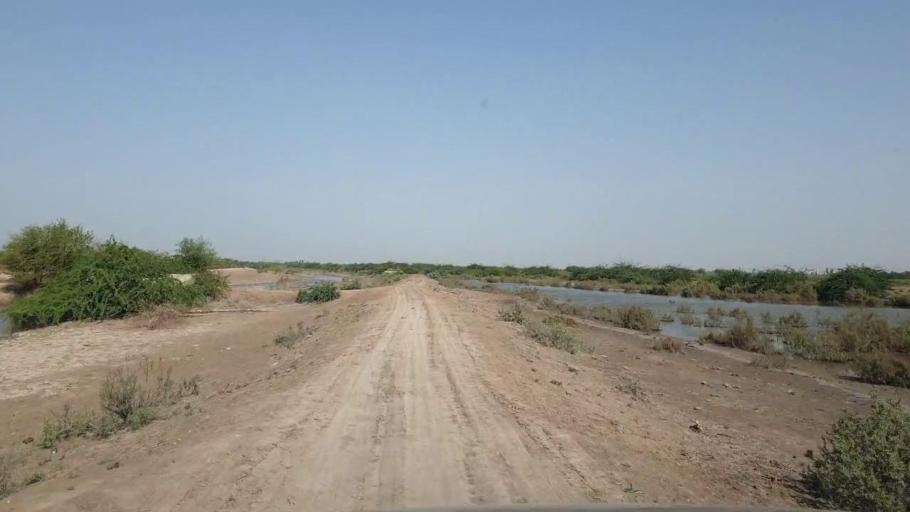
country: PK
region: Sindh
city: Tando Bago
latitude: 24.6558
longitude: 69.0703
